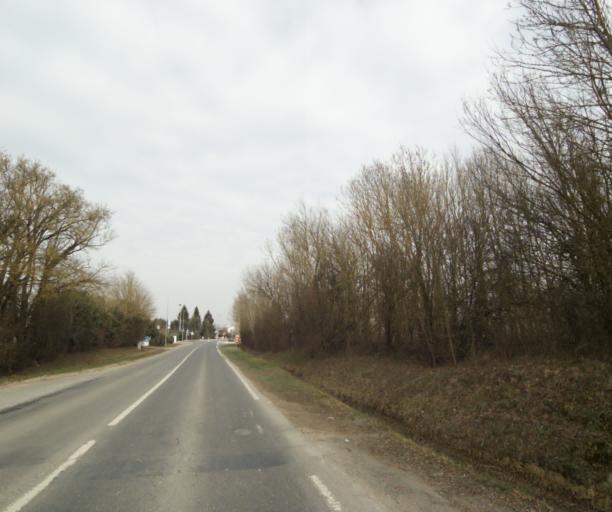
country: FR
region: Poitou-Charentes
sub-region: Departement des Deux-Sevres
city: Niort
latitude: 46.2954
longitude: -0.4590
